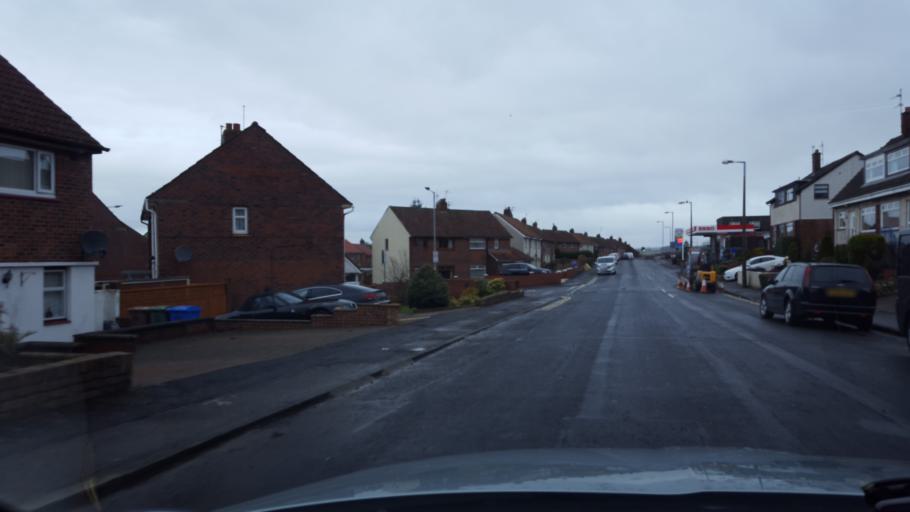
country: GB
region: Scotland
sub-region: South Ayrshire
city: Ayr
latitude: 55.4516
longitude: -4.6038
